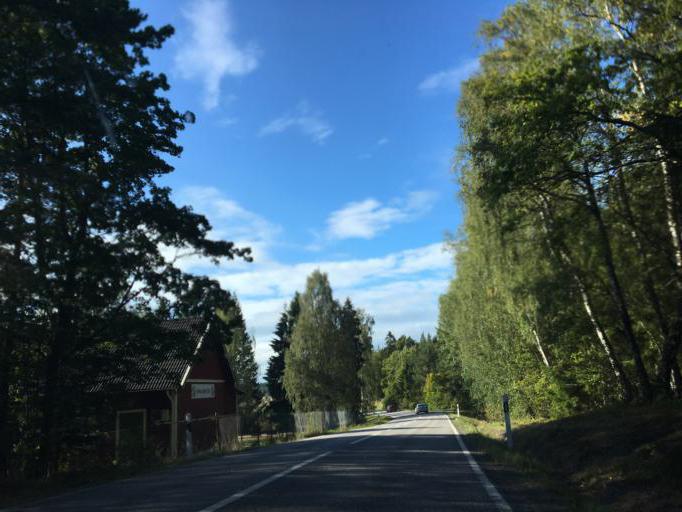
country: SE
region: Soedermanland
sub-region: Nykopings Kommun
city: Svalsta
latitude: 58.8649
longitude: 16.9070
